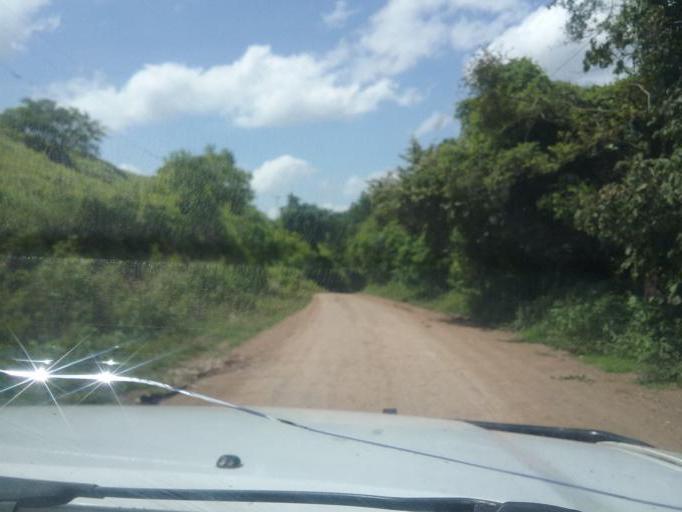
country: NI
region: Matagalpa
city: Terrabona
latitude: 12.7246
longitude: -85.9654
